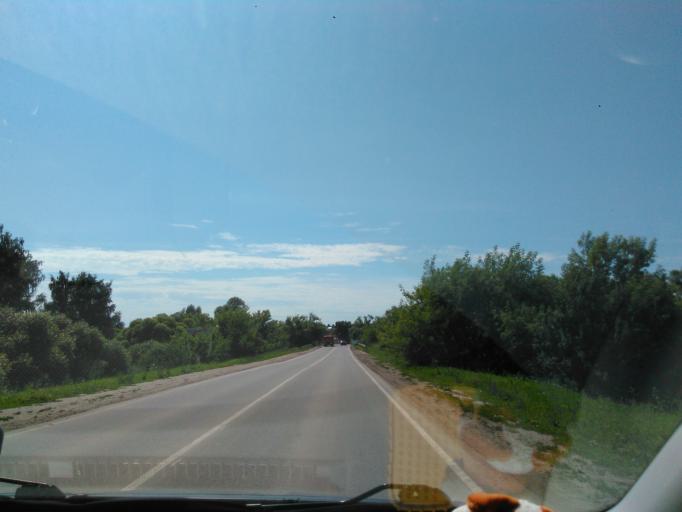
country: RU
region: Penza
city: Belinskiy
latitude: 52.9668
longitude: 43.4390
